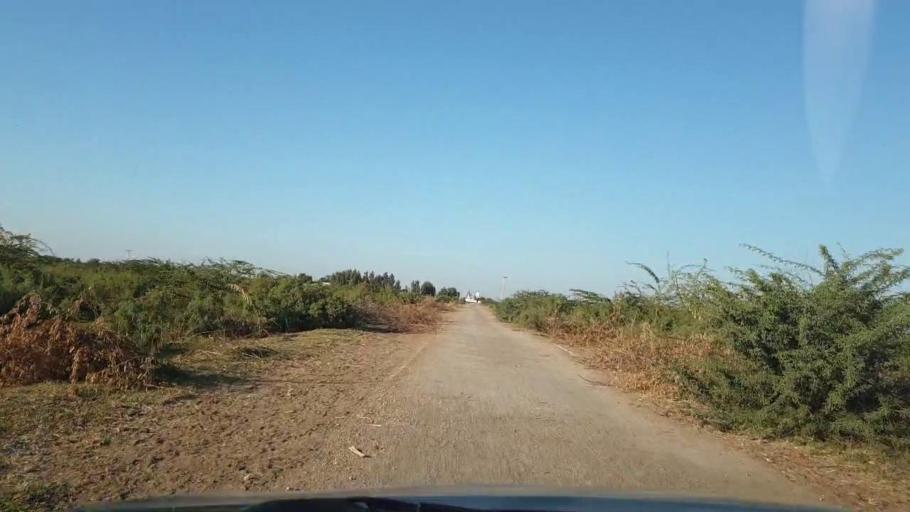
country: PK
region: Sindh
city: Jhol
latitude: 25.9056
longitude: 68.9251
